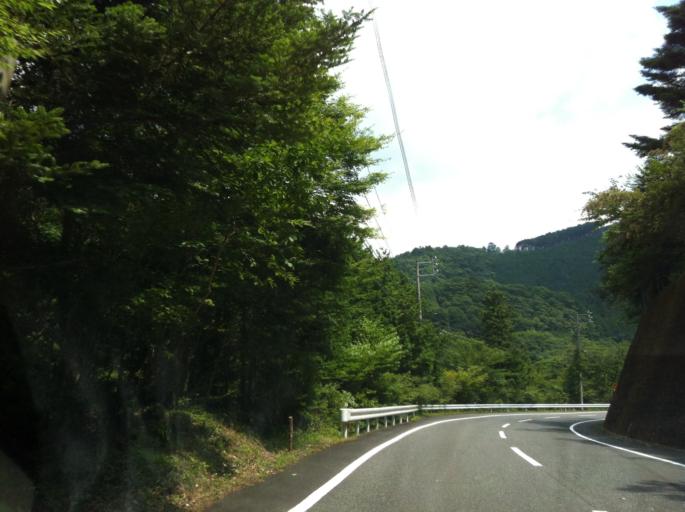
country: JP
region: Shizuoka
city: Fujinomiya
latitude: 35.2715
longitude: 138.3266
